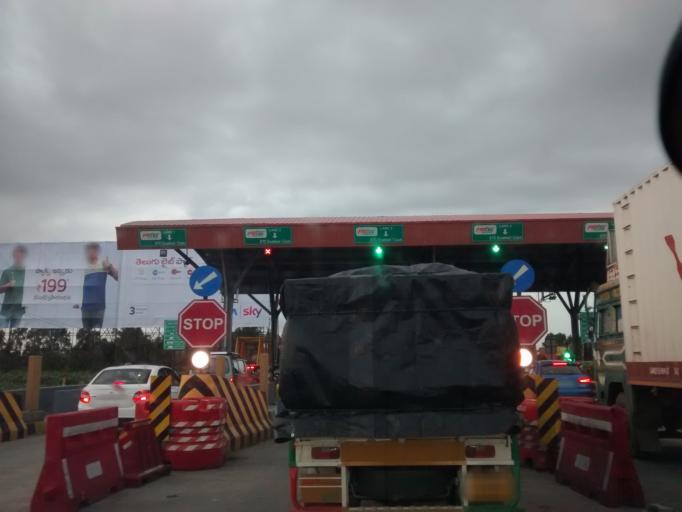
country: IN
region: Telangana
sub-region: Mahbubnagar
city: Farrukhnagar
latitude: 17.0061
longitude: 78.1944
